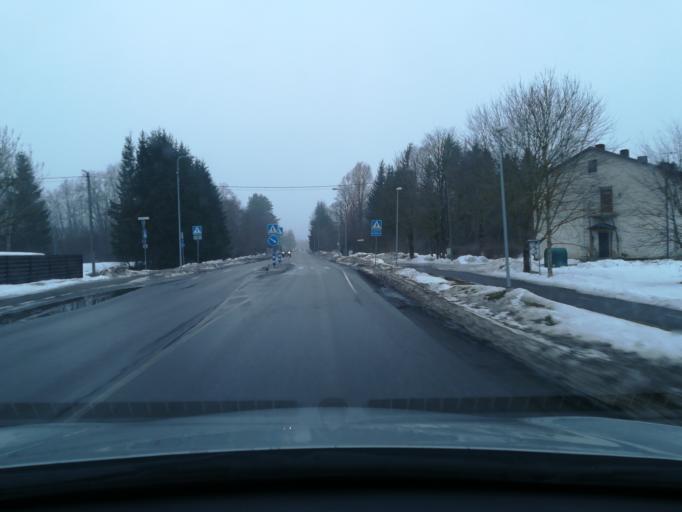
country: EE
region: Harju
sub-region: Rae vald
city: Jueri
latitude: 59.3620
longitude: 24.9385
